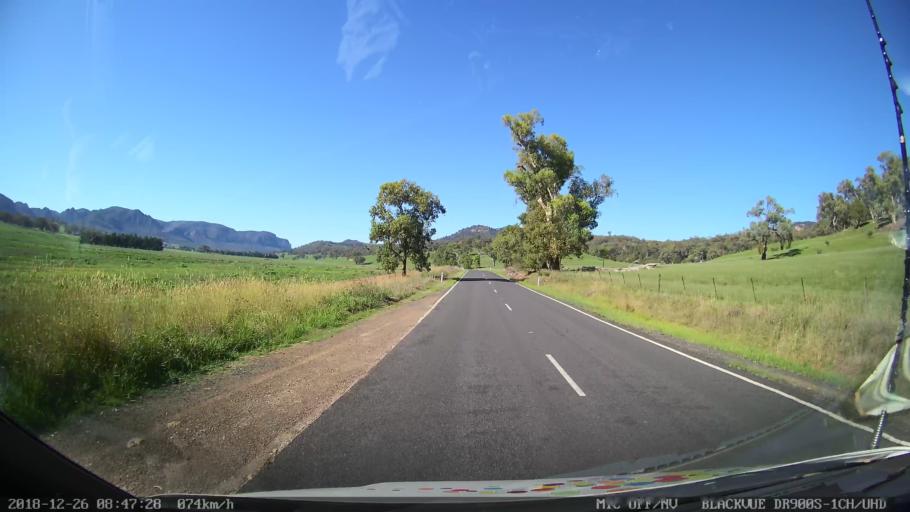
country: AU
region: New South Wales
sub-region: Mid-Western Regional
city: Kandos
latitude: -32.5429
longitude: 150.0913
